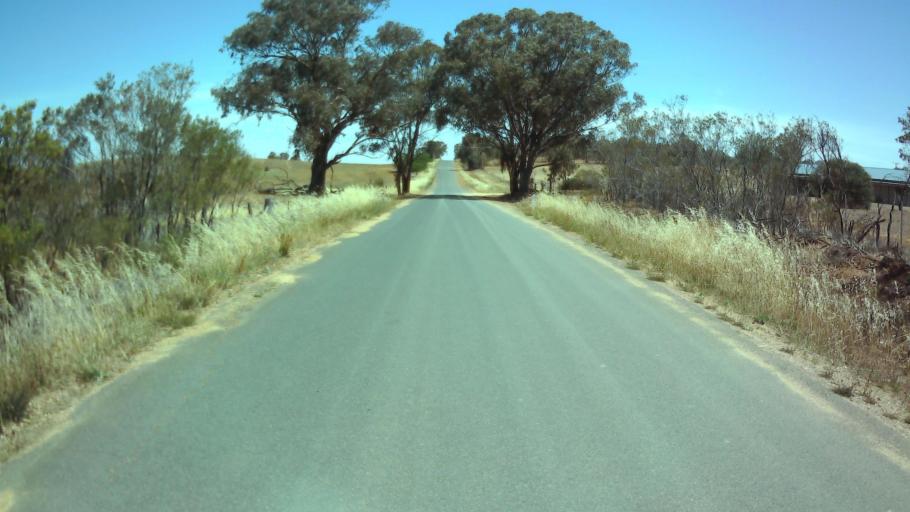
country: AU
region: New South Wales
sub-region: Weddin
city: Grenfell
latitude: -33.8996
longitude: 148.1850
